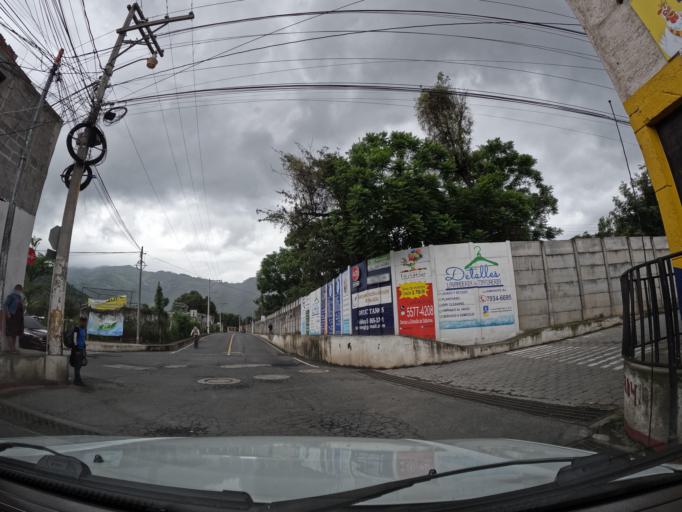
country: GT
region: Sacatepequez
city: Jocotenango
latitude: 14.5745
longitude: -90.7373
